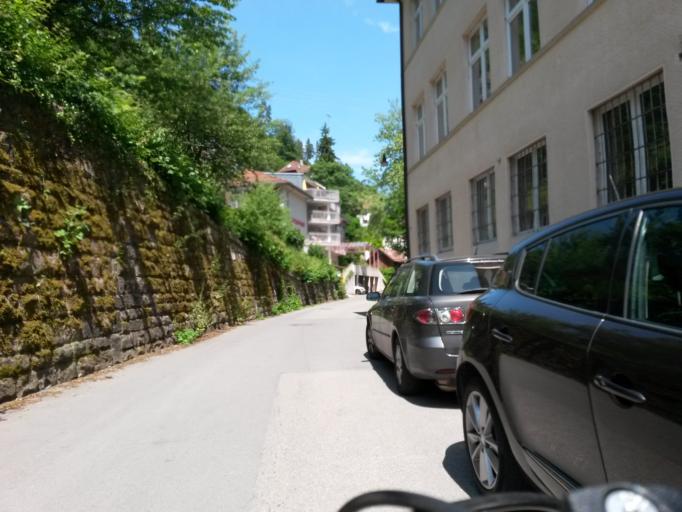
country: DE
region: Baden-Wuerttemberg
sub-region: Karlsruhe Region
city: Calw
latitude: 48.7044
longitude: 8.7325
